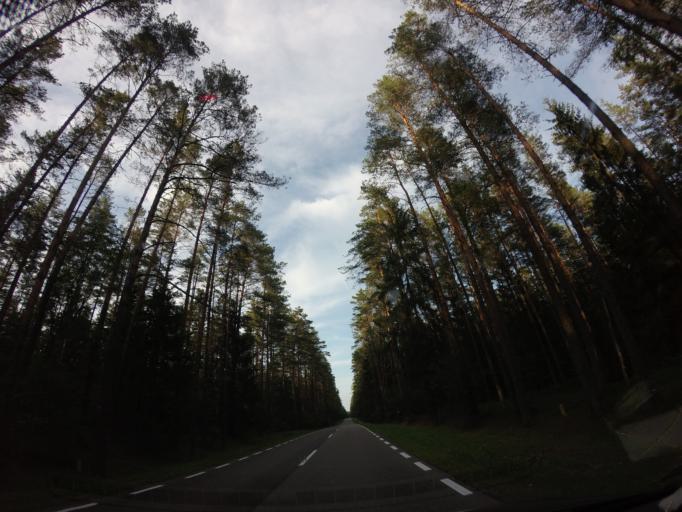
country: PL
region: Podlasie
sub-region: Powiat sejnenski
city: Krasnopol
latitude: 53.9690
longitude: 23.2498
